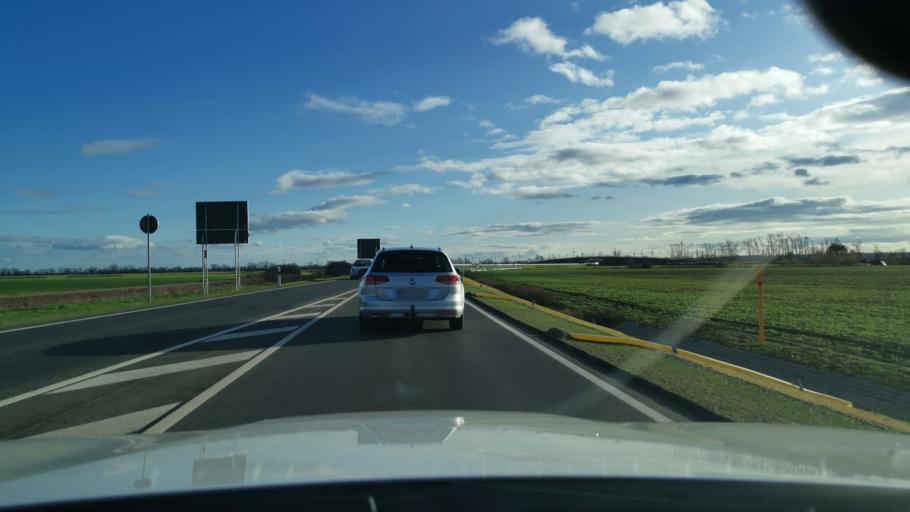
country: DE
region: Saxony-Anhalt
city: Wittenburg
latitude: 51.8254
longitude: 12.6412
